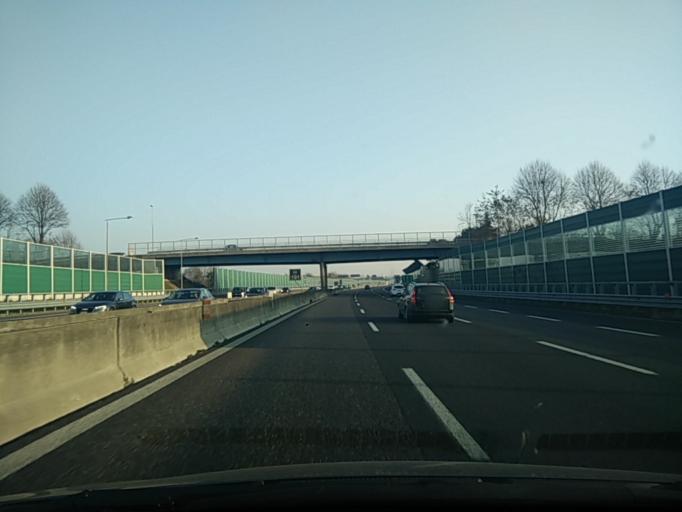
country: IT
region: Lombardy
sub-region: Provincia di Brescia
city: Capriolo
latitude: 45.6179
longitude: 9.9225
